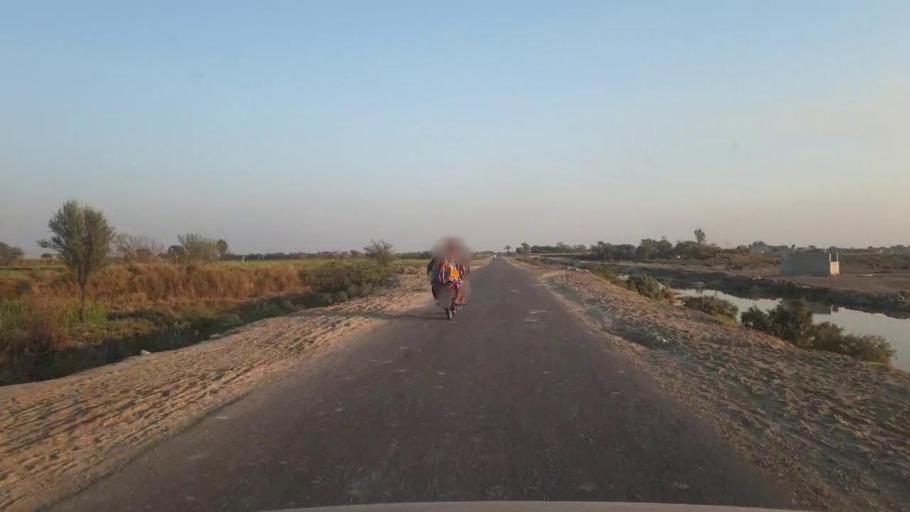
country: PK
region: Sindh
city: Chambar
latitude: 25.2831
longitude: 68.9111
